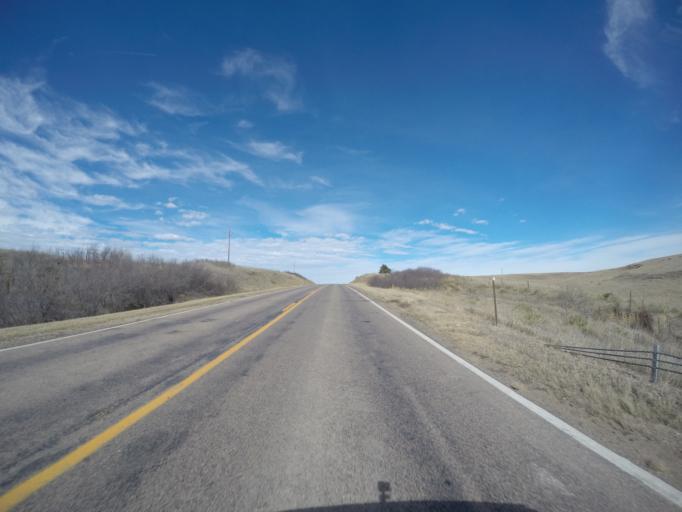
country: US
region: Nebraska
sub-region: Franklin County
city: Franklin
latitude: 40.1569
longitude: -98.9526
